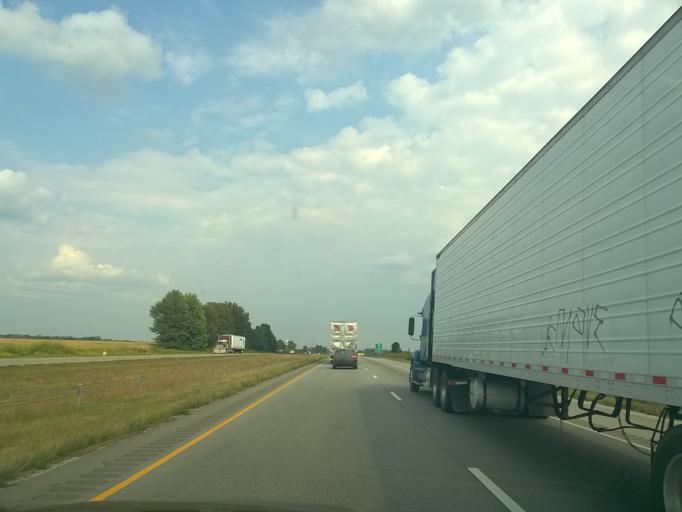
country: US
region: Indiana
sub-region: Clay County
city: Brazil
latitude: 39.4500
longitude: -87.1551
